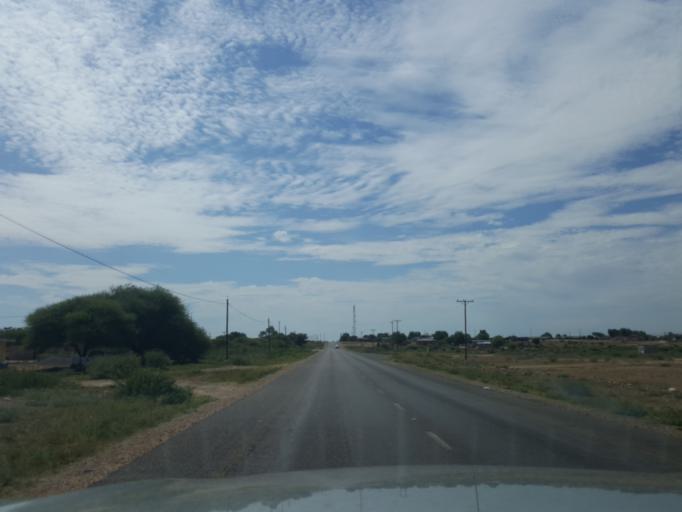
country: BW
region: Kweneng
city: Letlhakeng
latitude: -24.1100
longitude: 25.0346
